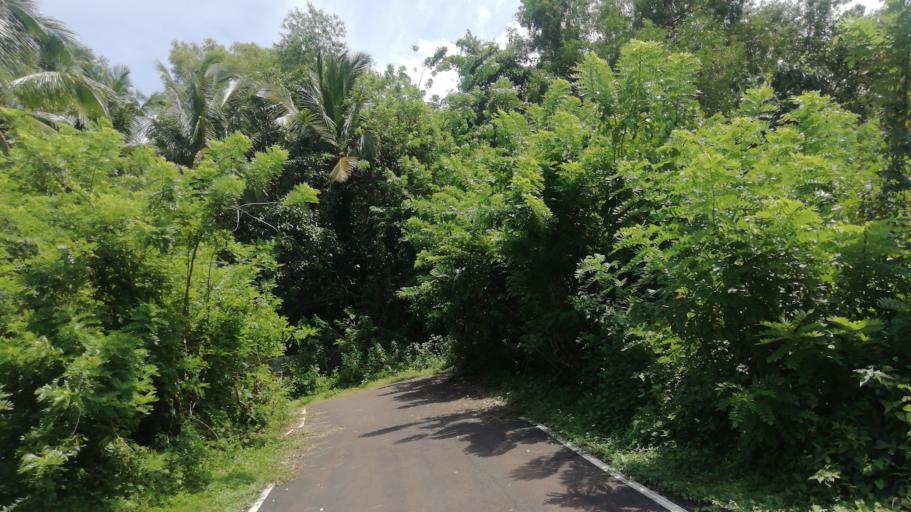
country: IN
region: Goa
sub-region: North Goa
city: Ponda
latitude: 15.3914
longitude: 74.0052
